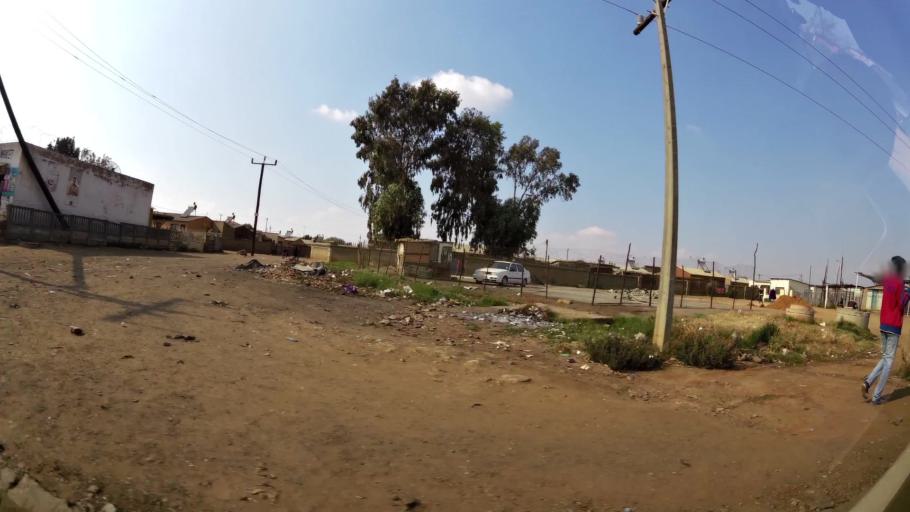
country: ZA
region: Gauteng
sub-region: Ekurhuleni Metropolitan Municipality
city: Springs
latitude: -26.1128
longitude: 28.4756
